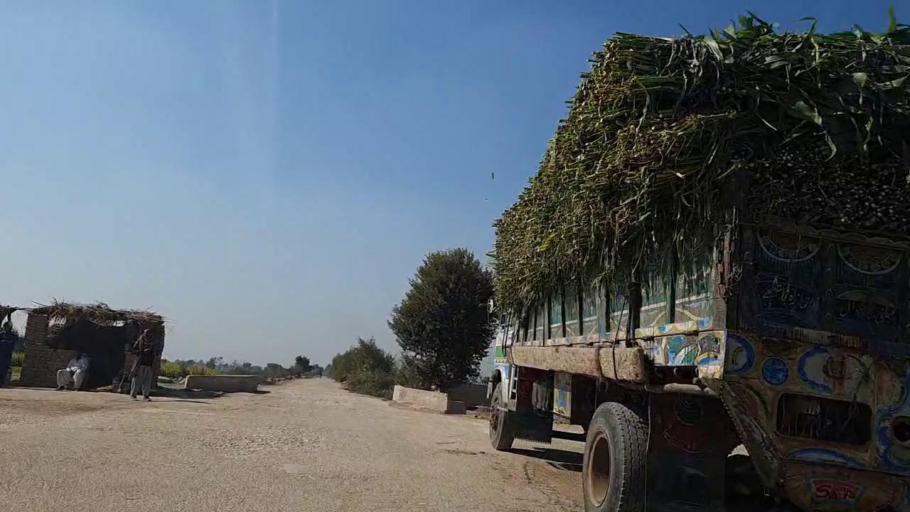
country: PK
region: Sindh
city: Daulatpur
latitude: 26.2906
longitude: 68.0797
